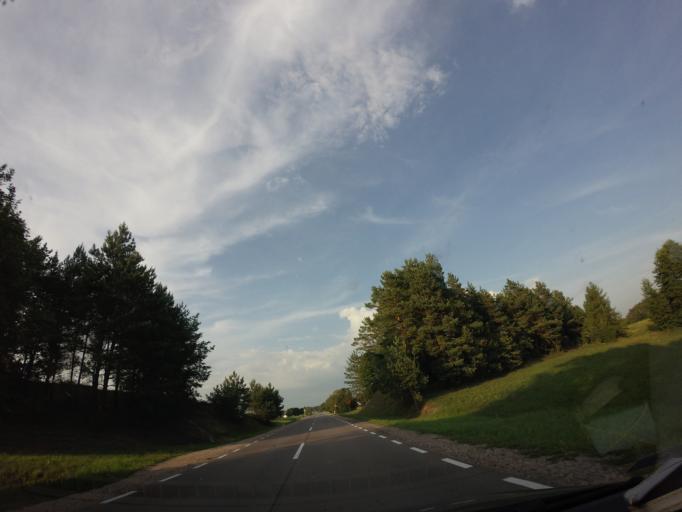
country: PL
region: Podlasie
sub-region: Powiat sejnenski
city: Sejny
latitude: 54.1297
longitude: 23.4519
